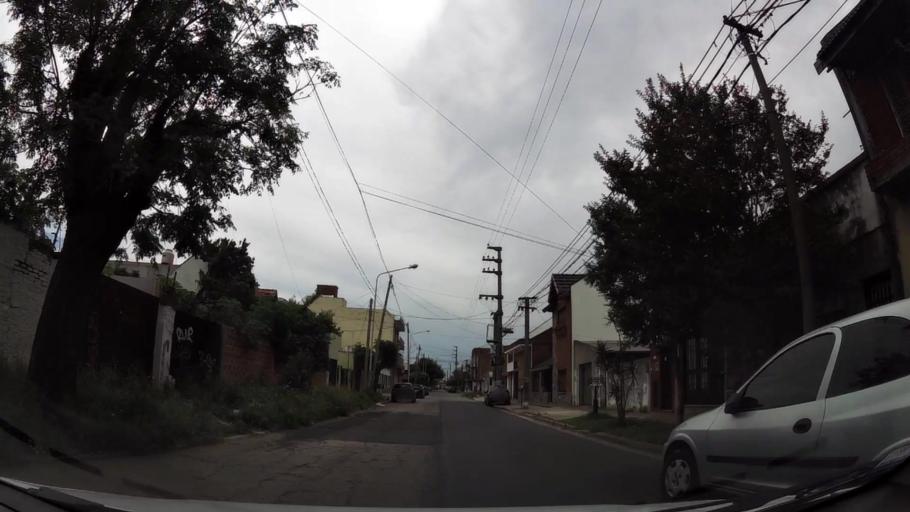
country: AR
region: Buenos Aires
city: San Justo
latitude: -34.6653
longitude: -58.5352
